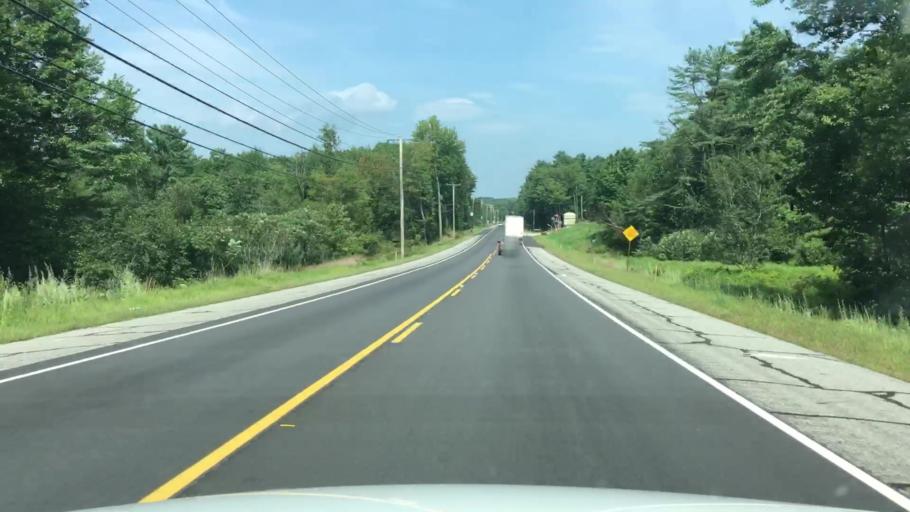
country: US
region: Maine
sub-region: Androscoggin County
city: Turner
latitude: 44.2082
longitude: -70.2458
